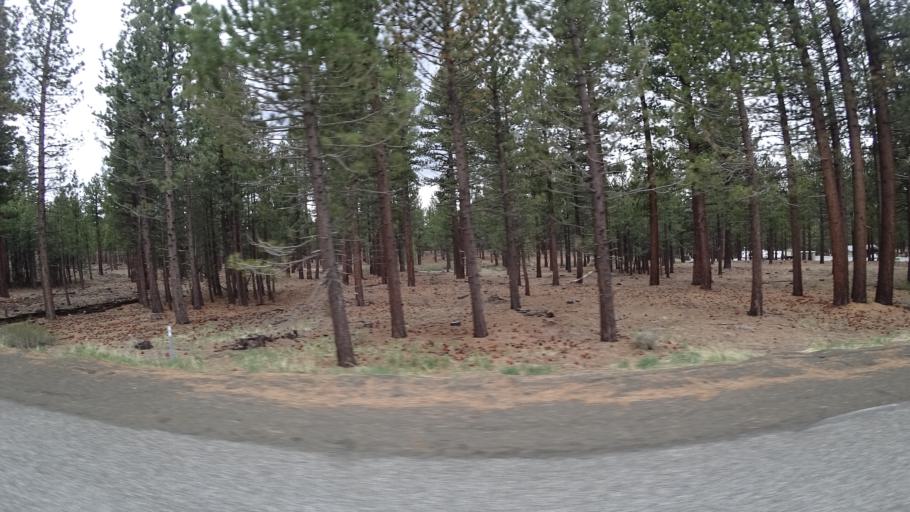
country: US
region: California
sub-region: Mono County
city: Mammoth Lakes
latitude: 37.7307
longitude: -118.9675
